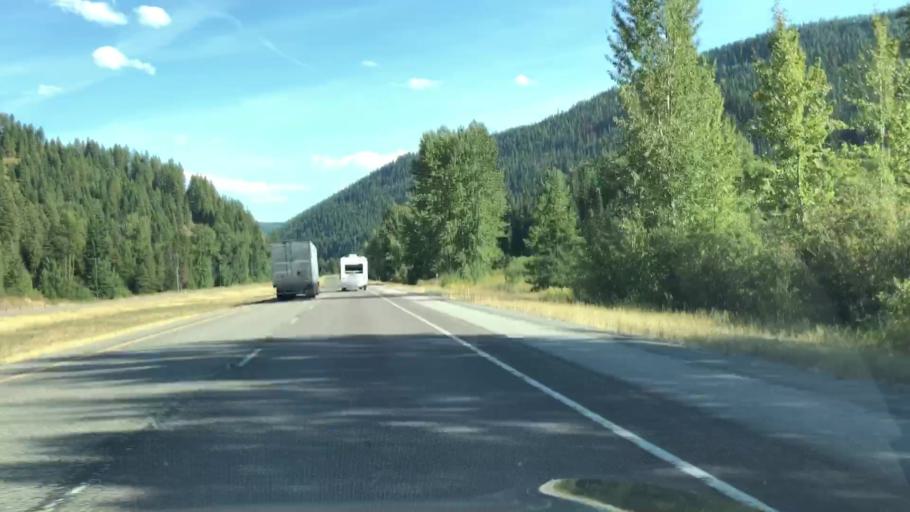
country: US
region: Montana
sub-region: Sanders County
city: Thompson Falls
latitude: 47.3643
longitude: -115.3267
